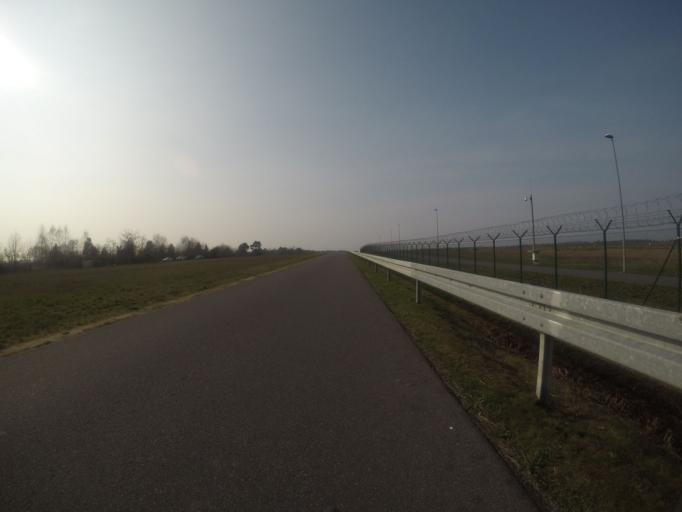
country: DE
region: Brandenburg
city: Rangsdorf
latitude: 52.3413
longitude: 13.4585
